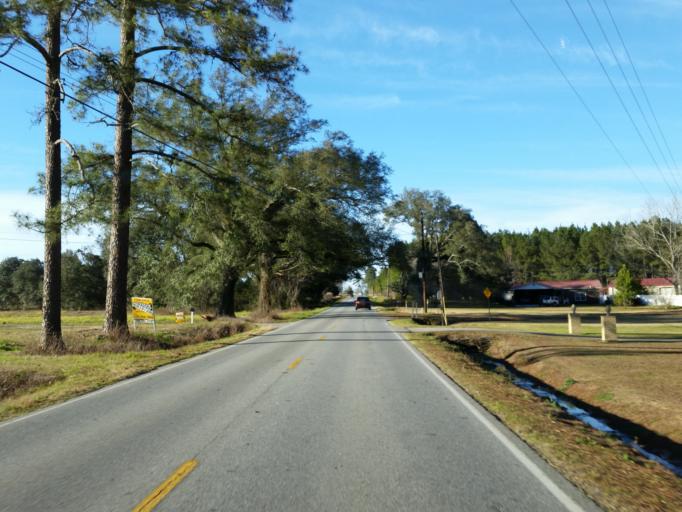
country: US
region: Georgia
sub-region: Lowndes County
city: Hahira
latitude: 30.9463
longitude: -83.3512
